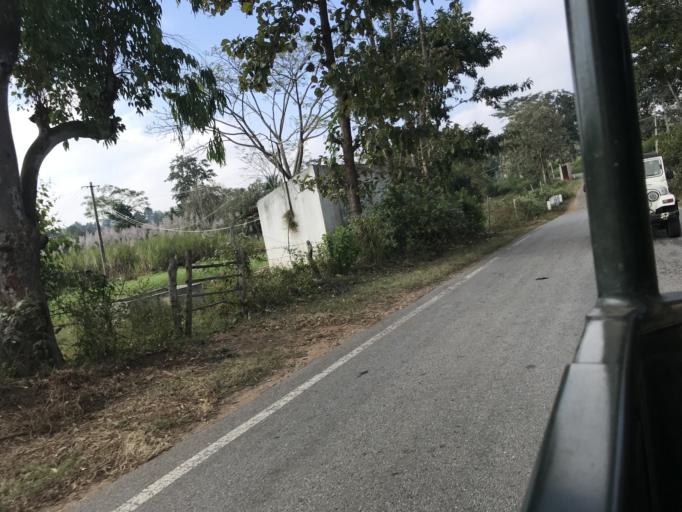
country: IN
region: Karnataka
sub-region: Mysore
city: Heggadadevankote
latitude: 11.9476
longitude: 76.2479
